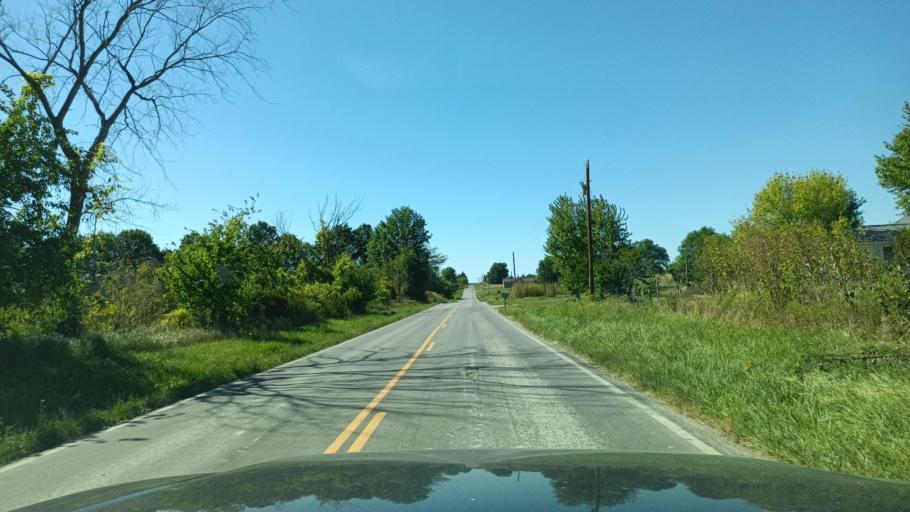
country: US
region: Missouri
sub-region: Macon County
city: La Plata
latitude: 40.0223
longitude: -92.5555
